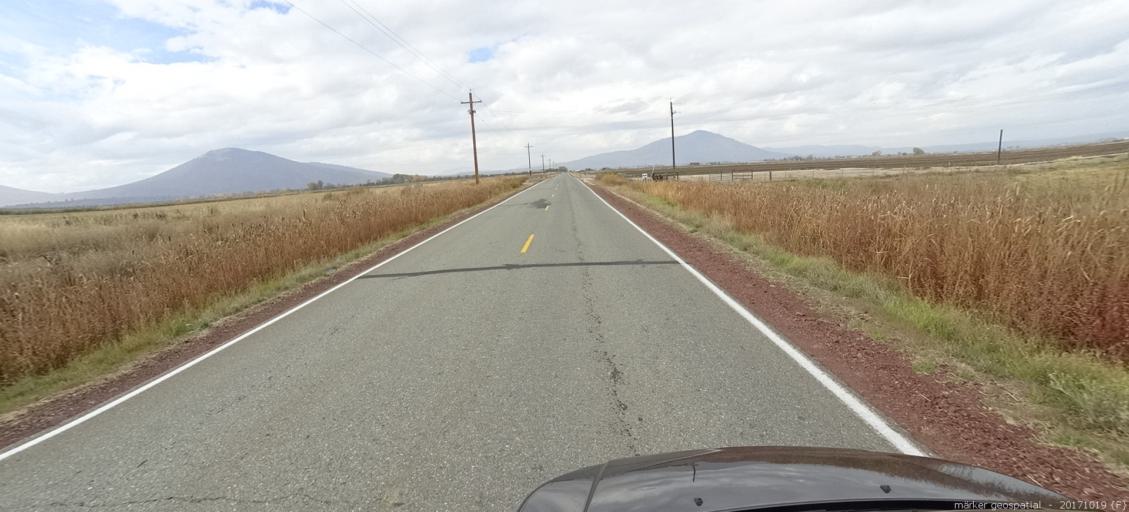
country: US
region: California
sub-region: Shasta County
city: Burney
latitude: 41.0509
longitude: -121.4314
